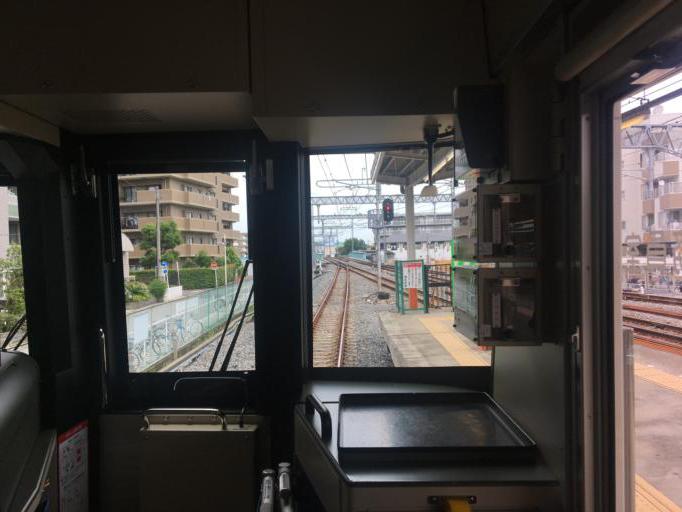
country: JP
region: Saitama
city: Koshigaya
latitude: 35.9364
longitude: 139.7743
